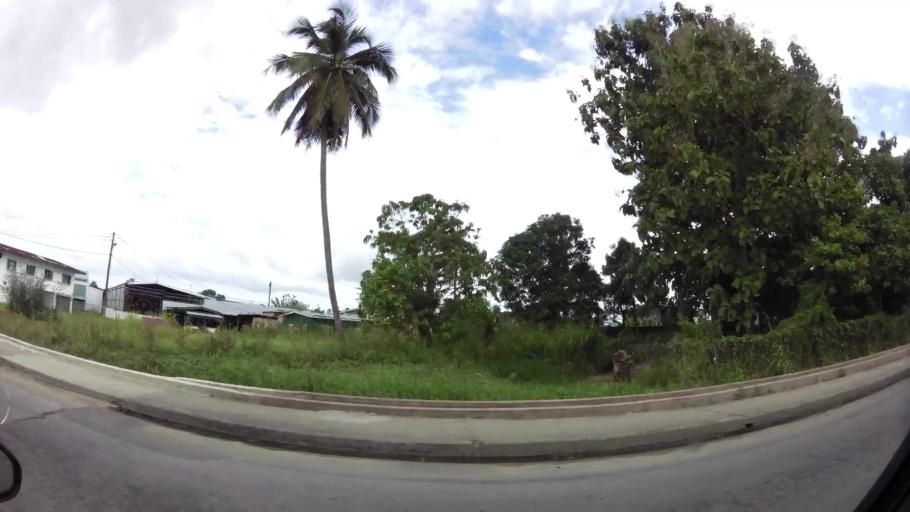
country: TT
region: Chaguanas
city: Chaguanas
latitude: 10.4631
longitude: -61.4225
